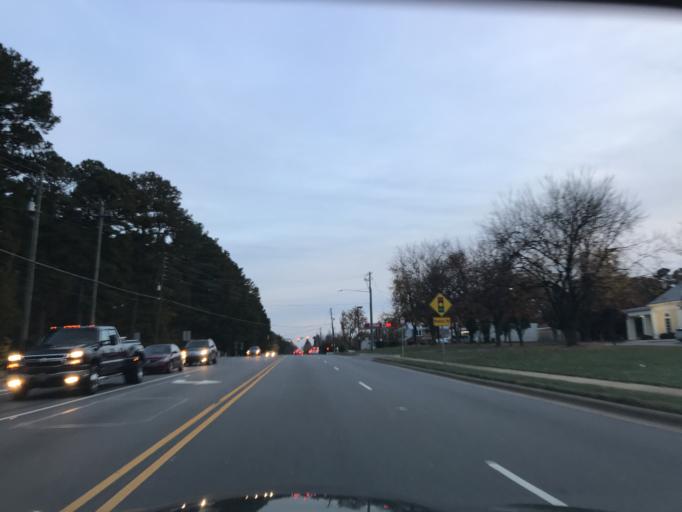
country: US
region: North Carolina
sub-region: Wake County
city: West Raleigh
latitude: 35.8813
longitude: -78.6259
